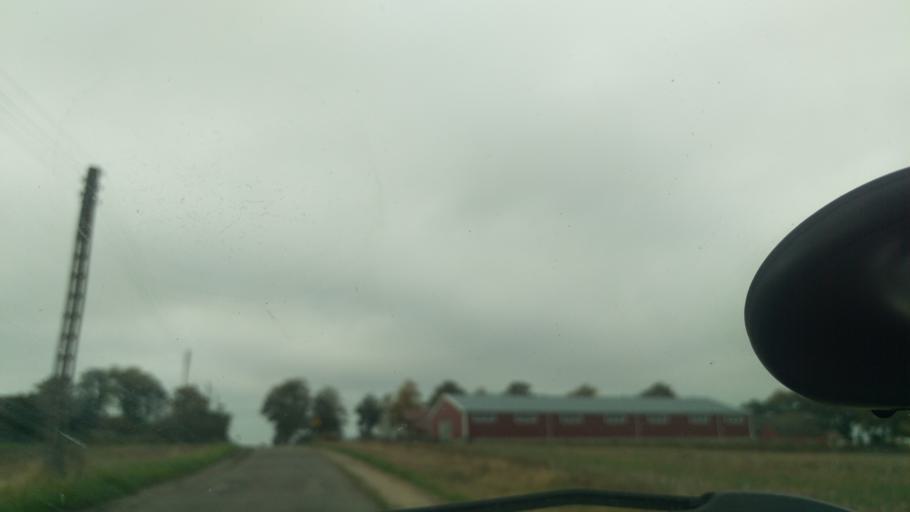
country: PL
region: West Pomeranian Voivodeship
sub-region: Powiat pyrzycki
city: Przelewice
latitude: 53.0749
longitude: 15.0971
